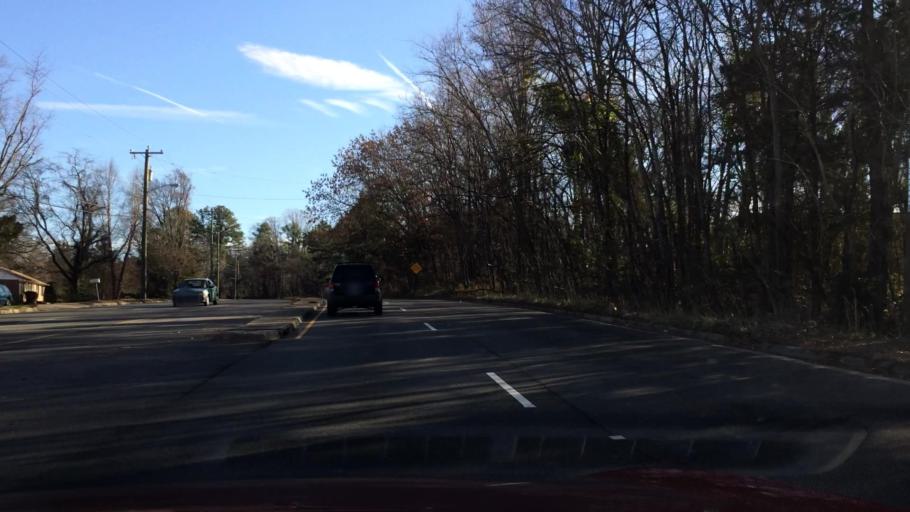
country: US
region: Virginia
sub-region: Chesterfield County
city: Bon Air
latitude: 37.5329
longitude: -77.5072
